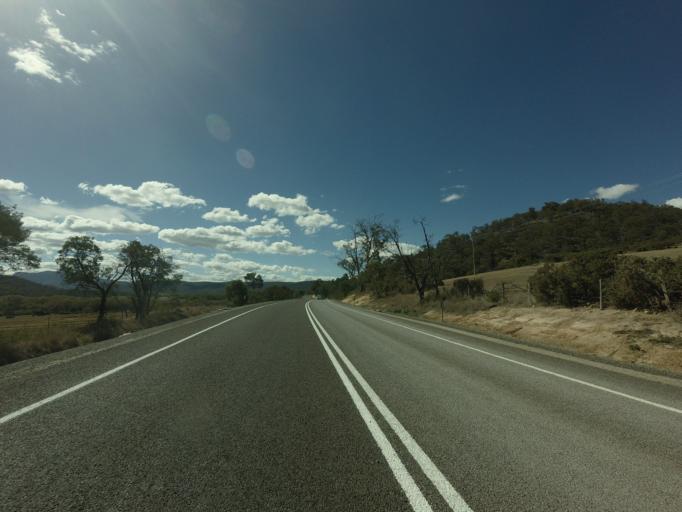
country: AU
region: Tasmania
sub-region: Break O'Day
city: St Helens
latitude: -41.6614
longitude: 147.9142
